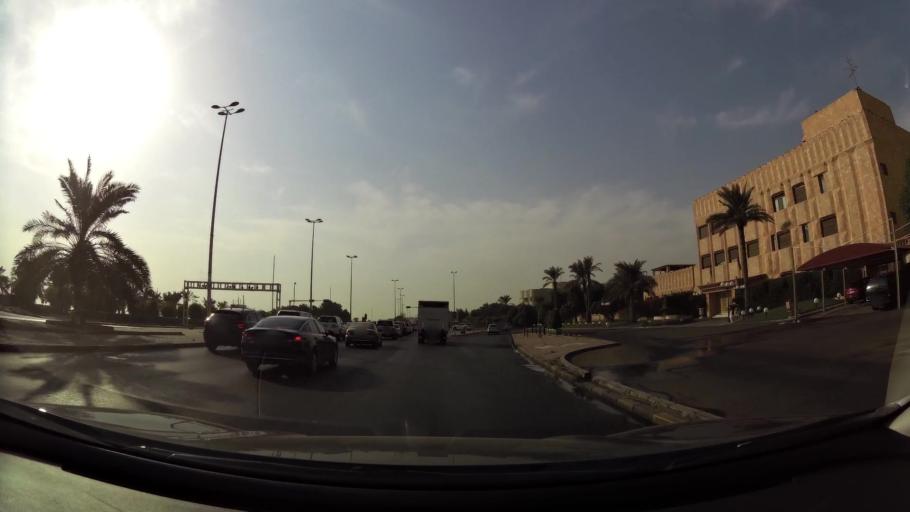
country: KW
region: Muhafazat Hawalli
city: Salwa
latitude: 29.2811
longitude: 48.0874
